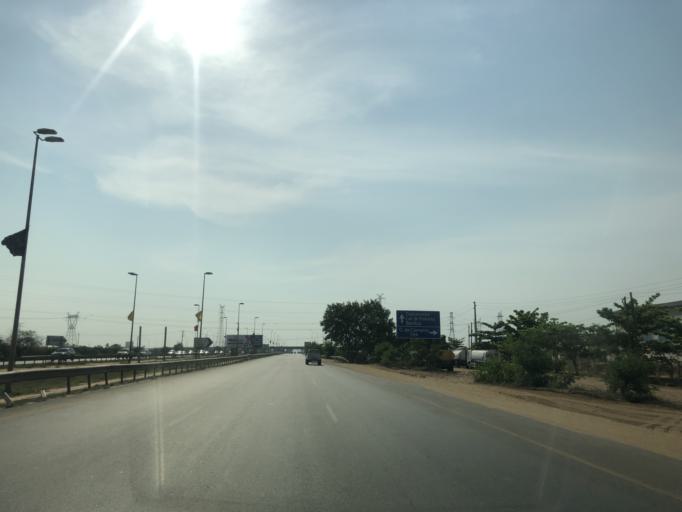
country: AO
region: Luanda
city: Luanda
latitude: -8.9732
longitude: 13.2608
